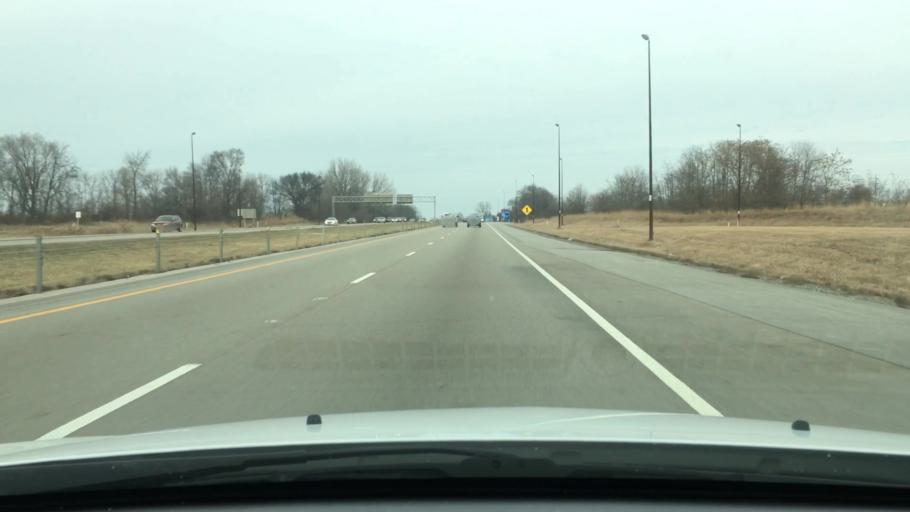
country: US
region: Illinois
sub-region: Sangamon County
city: Grandview
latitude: 39.8033
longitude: -89.5947
